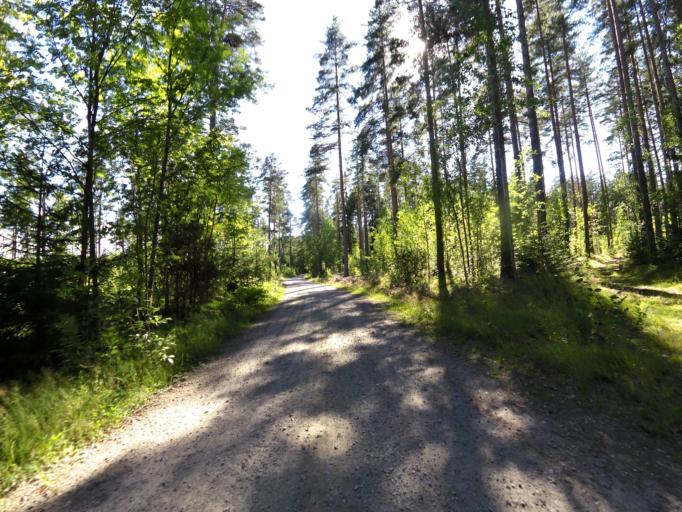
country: SE
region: Gaevleborg
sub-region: Hofors Kommun
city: Hofors
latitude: 60.5751
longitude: 16.4280
